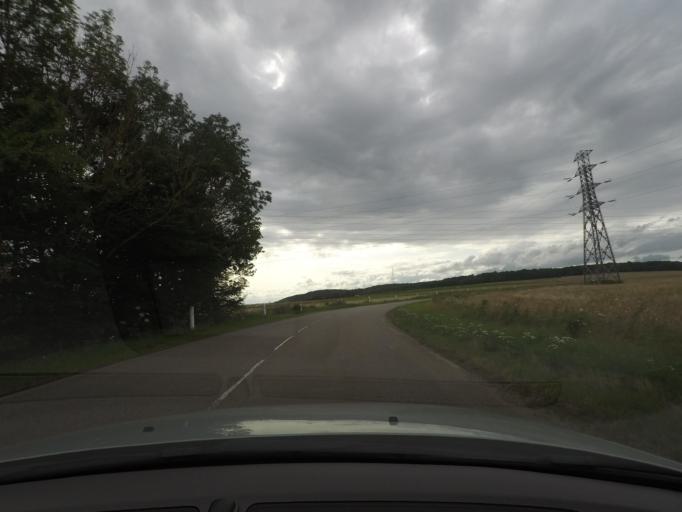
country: FR
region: Haute-Normandie
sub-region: Departement de l'Eure
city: Le Manoir
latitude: 49.3272
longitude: 1.2163
